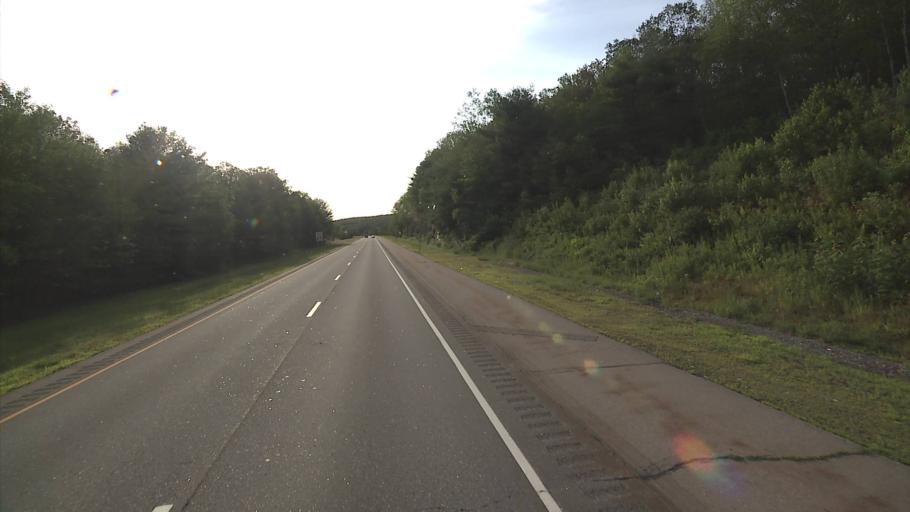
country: US
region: Connecticut
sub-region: New London County
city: Colchester
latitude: 41.5659
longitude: -72.2512
